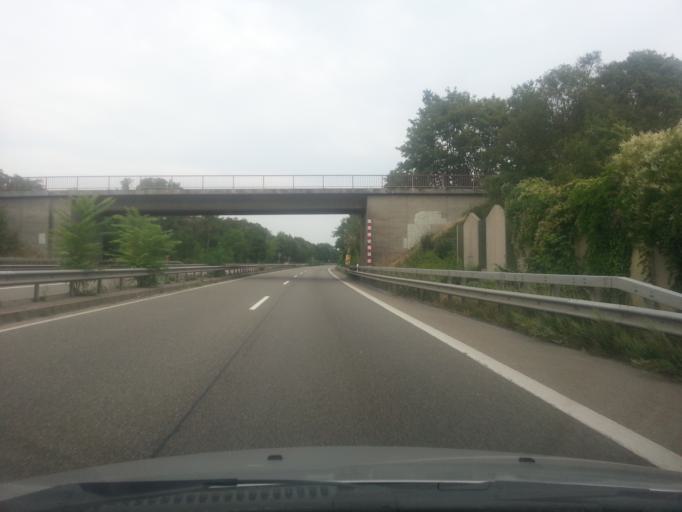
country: DE
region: Rheinland-Pfalz
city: Dudenhofen
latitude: 49.3303
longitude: 8.4092
